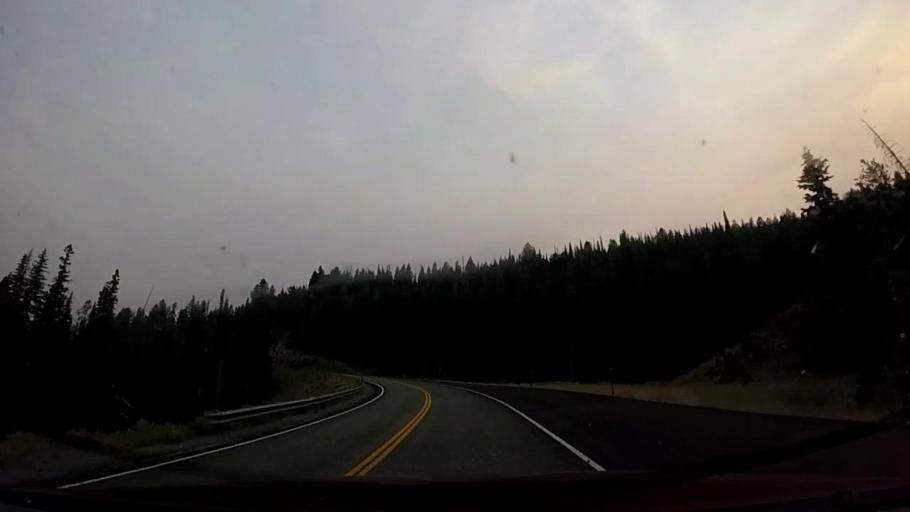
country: US
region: Idaho
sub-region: Blaine County
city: Ketchum
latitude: 43.8864
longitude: -114.6970
